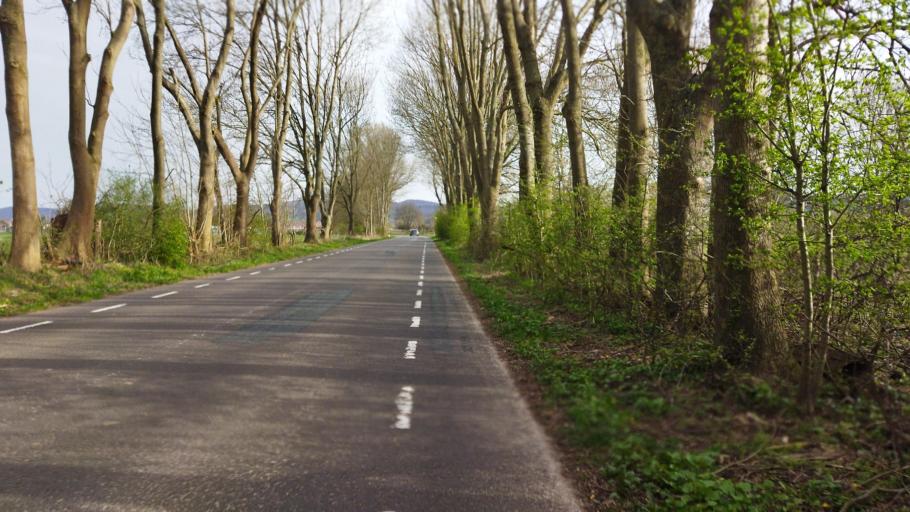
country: DE
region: Lower Saxony
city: Rinteln
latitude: 52.1886
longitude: 9.0269
